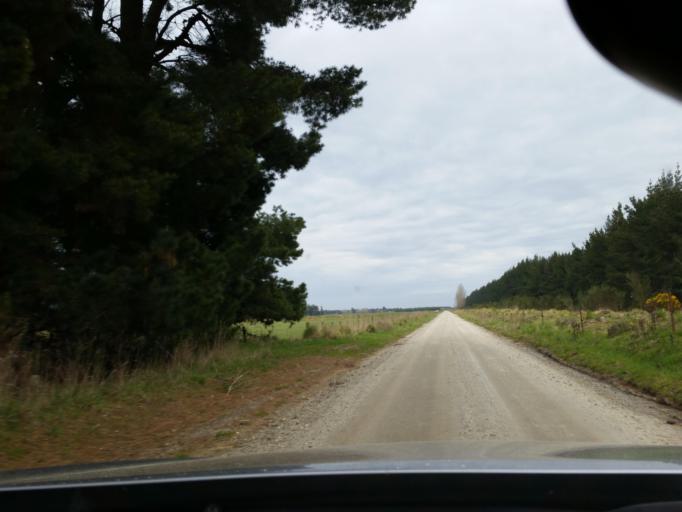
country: NZ
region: Southland
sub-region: Southland District
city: Winton
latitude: -46.2221
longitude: 168.4930
